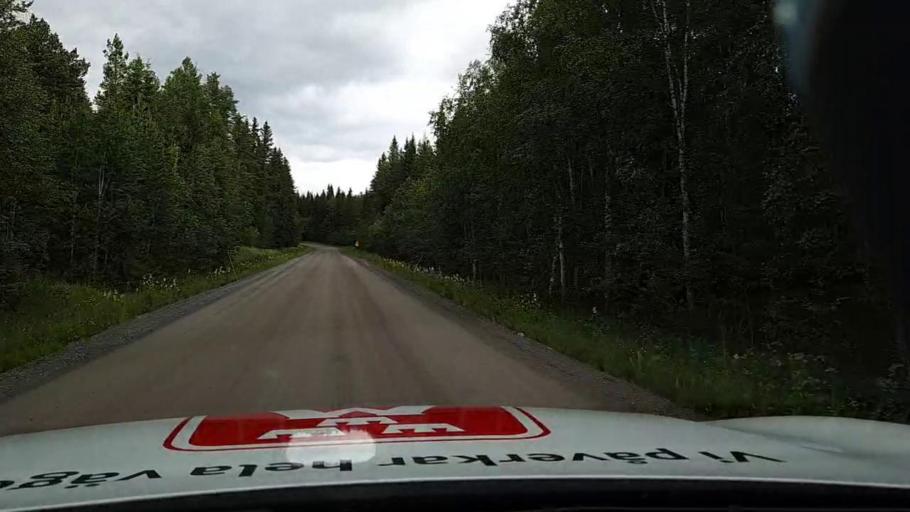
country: SE
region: Vaesternorrland
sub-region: Solleftea Kommun
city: As
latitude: 63.5074
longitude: 16.3614
